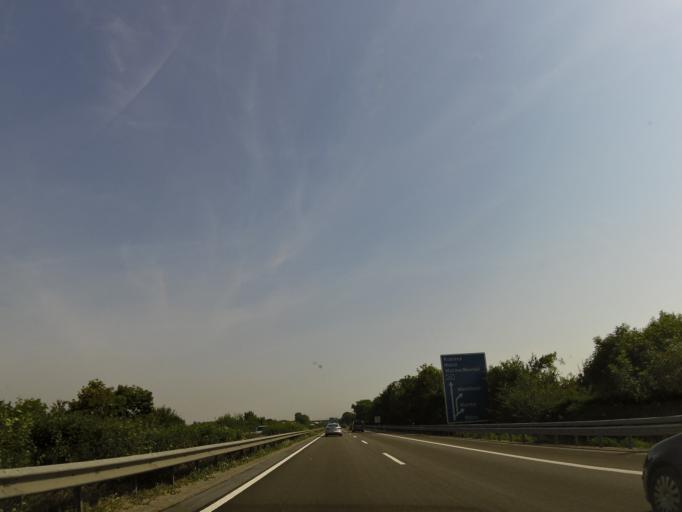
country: DE
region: Rheinland-Pfalz
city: Kleinniedesheim
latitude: 49.6138
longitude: 8.2917
